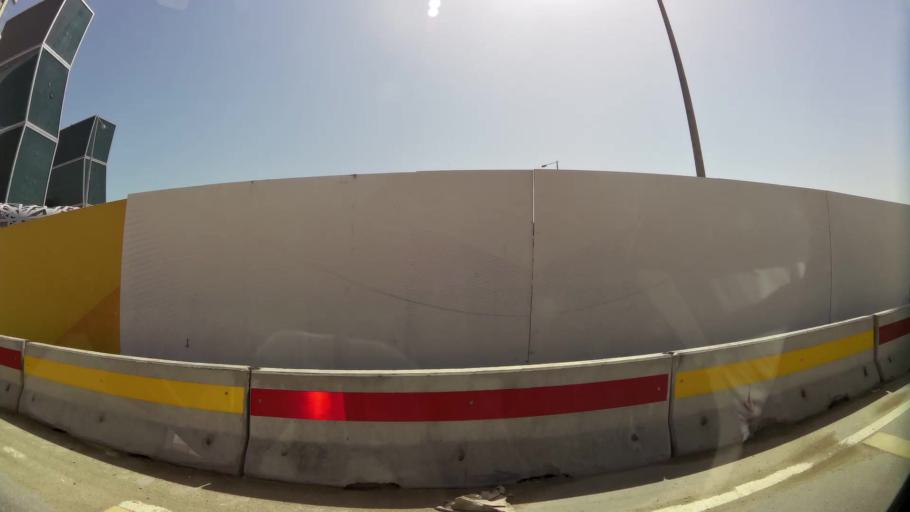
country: QA
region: Baladiyat ad Dawhah
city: Doha
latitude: 25.3762
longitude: 51.5229
